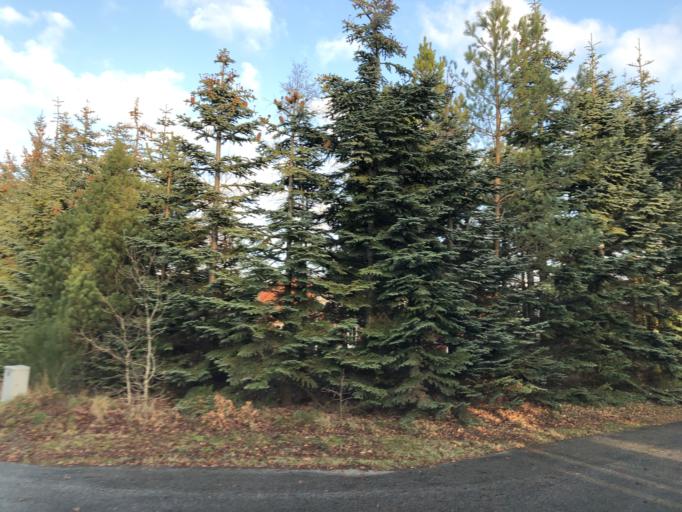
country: DK
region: Central Jutland
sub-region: Holstebro Kommune
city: Ulfborg
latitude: 56.3191
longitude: 8.4335
